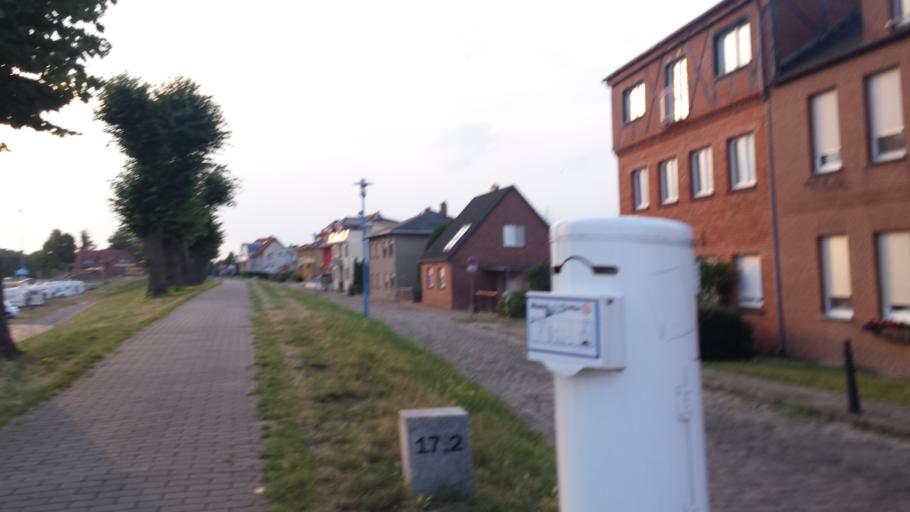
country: DE
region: Brandenburg
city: Wittenberge
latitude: 52.9901
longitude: 11.7478
